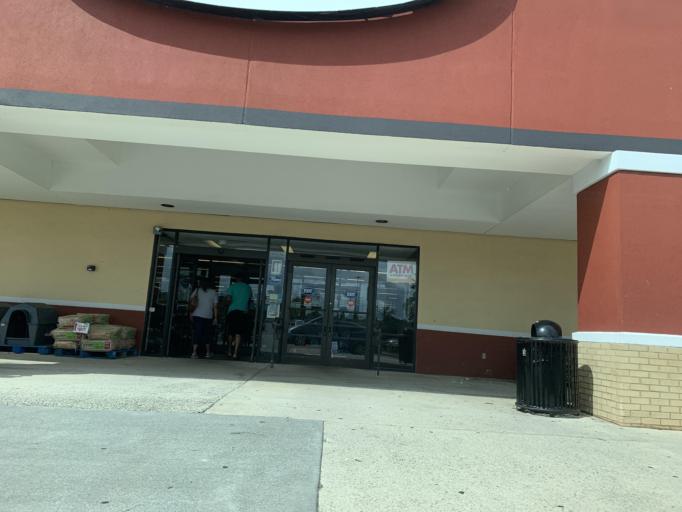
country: US
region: North Carolina
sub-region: Durham County
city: Durham
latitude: 35.9097
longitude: -78.9403
